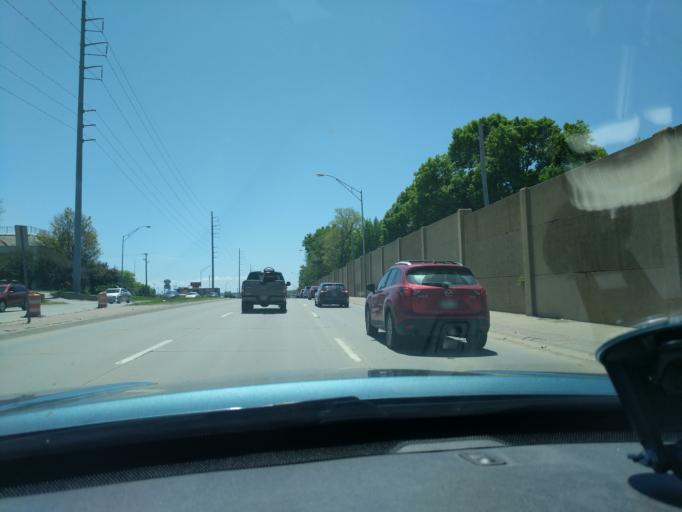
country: US
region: Nebraska
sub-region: Douglas County
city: Ralston
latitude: 41.2302
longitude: -96.0240
